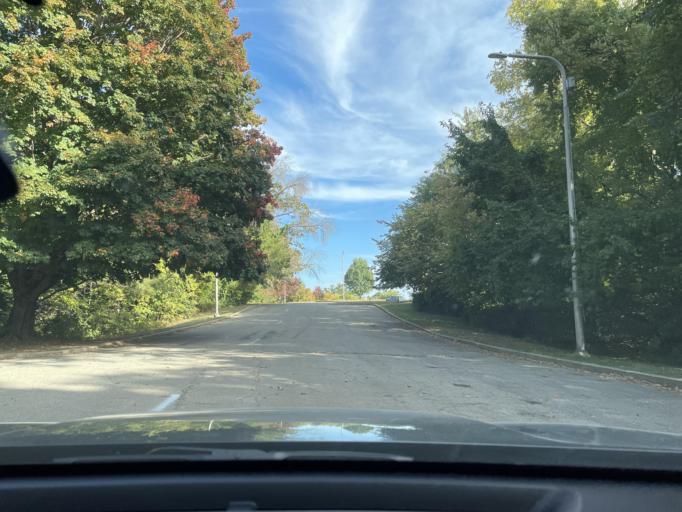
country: US
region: Missouri
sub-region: Buchanan County
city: Saint Joseph
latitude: 39.8011
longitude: -94.8535
